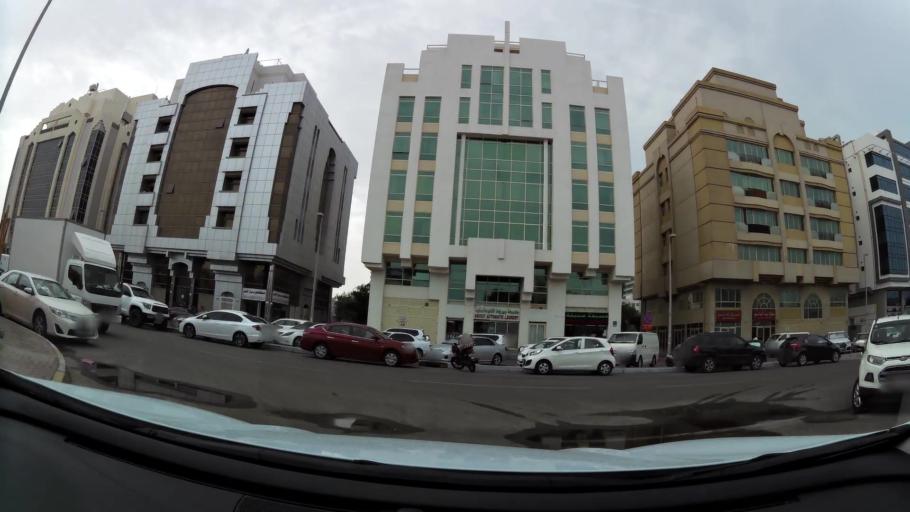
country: AE
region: Abu Dhabi
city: Abu Dhabi
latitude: 24.4341
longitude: 54.4375
